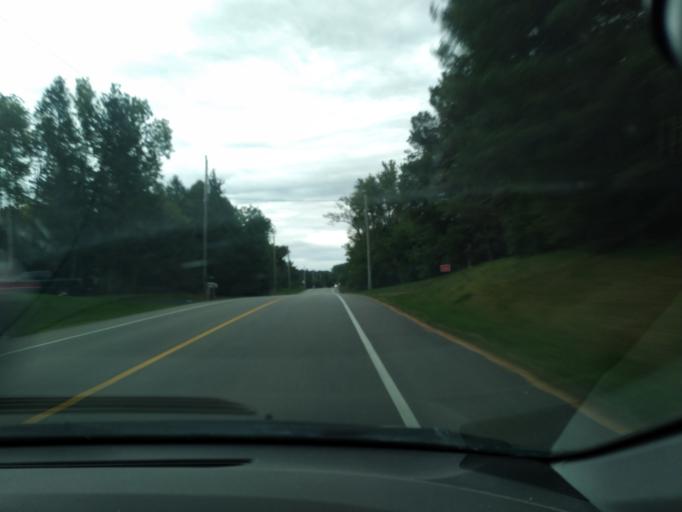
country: CA
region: Ontario
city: Bradford West Gwillimbury
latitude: 43.9756
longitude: -79.7988
